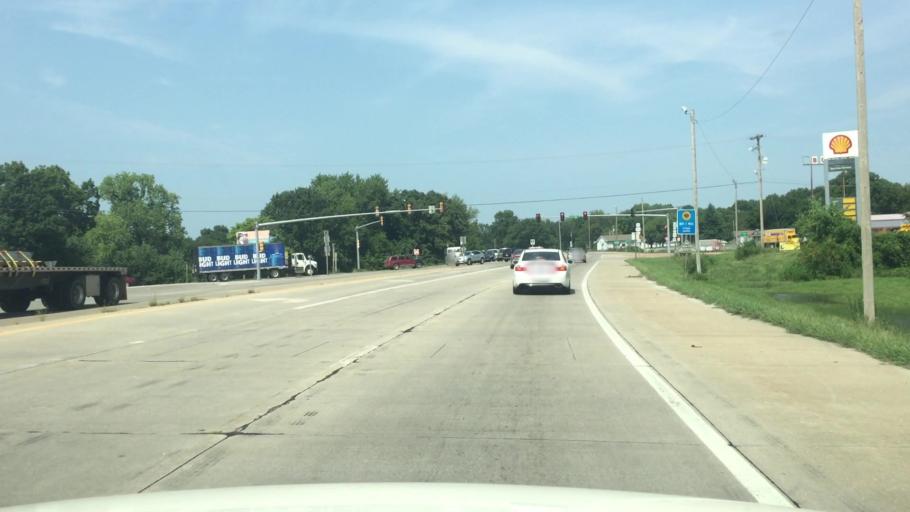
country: US
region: Kansas
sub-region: Crawford County
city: Pittsburg
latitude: 37.4103
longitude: -94.7243
